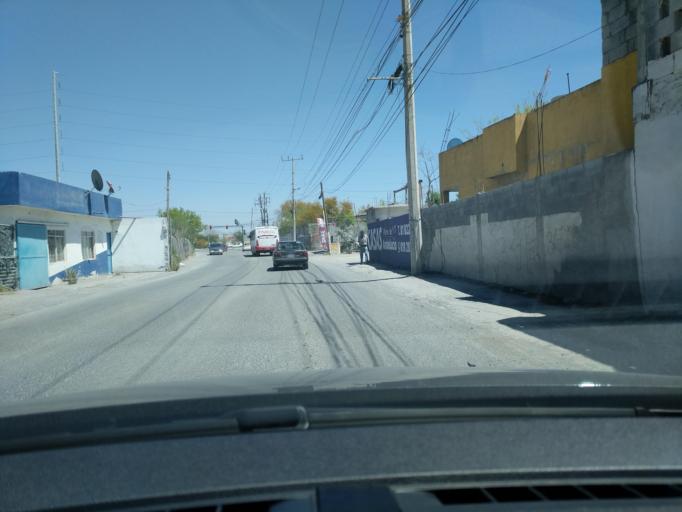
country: MX
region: Nuevo Leon
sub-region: Salinas Victoria
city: Emiliano Zapata
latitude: 25.9102
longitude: -100.2681
